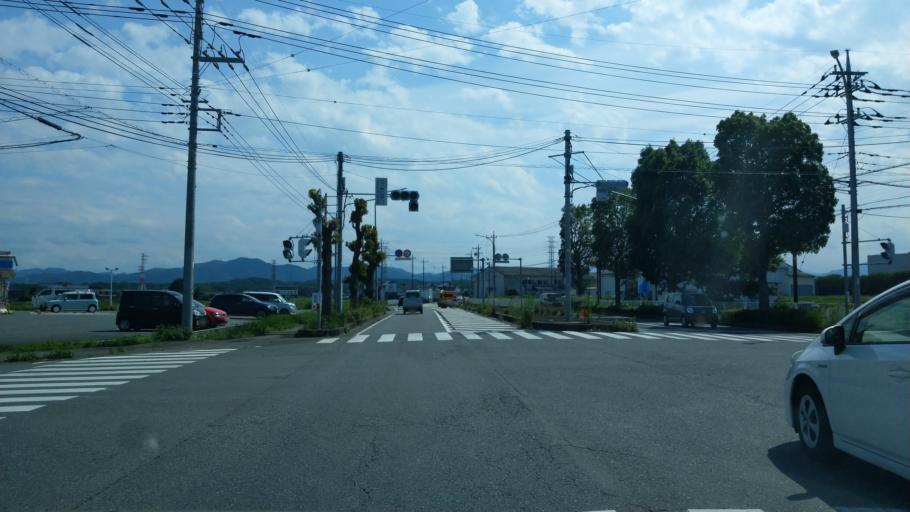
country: JP
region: Saitama
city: Honjo
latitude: 36.2185
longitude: 139.1619
